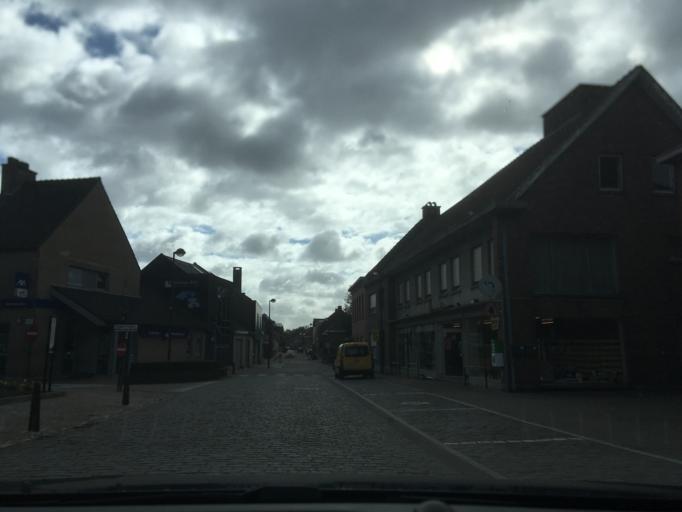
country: BE
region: Flanders
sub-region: Provincie West-Vlaanderen
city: Hooglede
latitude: 50.9967
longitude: 3.0956
